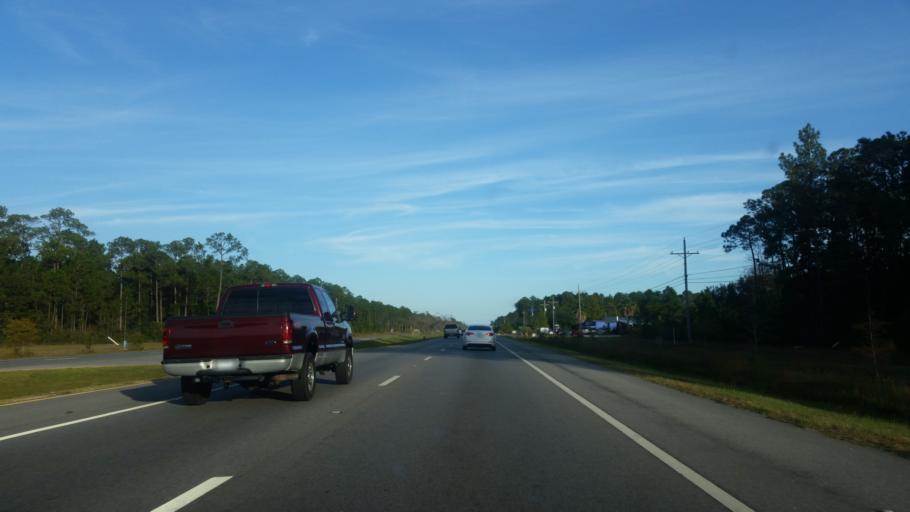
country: US
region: Mississippi
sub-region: Jackson County
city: Gulf Park Estates
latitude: 30.4048
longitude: -88.7346
